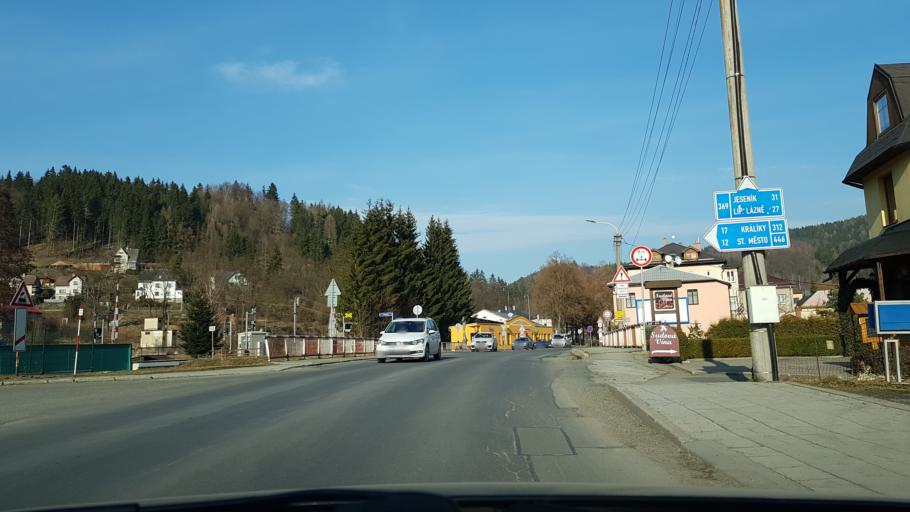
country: CZ
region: Olomoucky
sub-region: Okres Sumperk
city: Hanusovice
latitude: 50.0774
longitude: 16.9329
